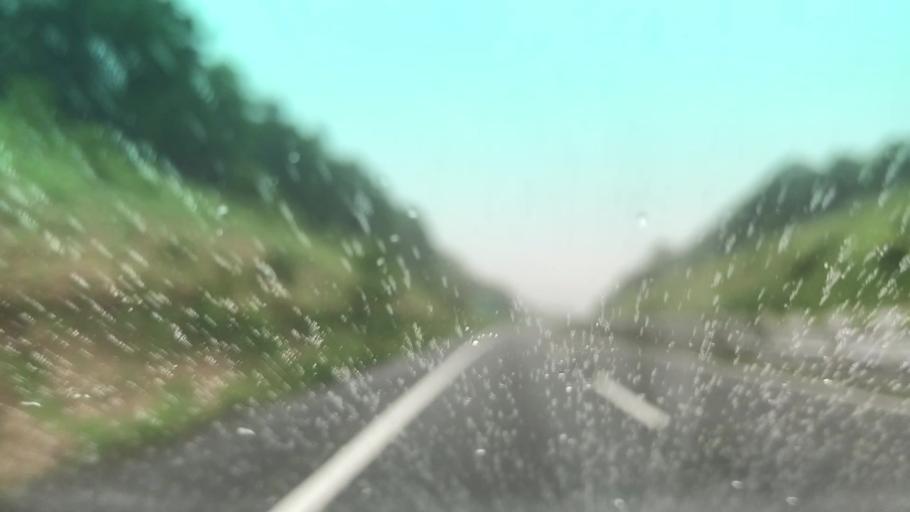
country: JP
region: Hokkaido
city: Tomakomai
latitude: 42.6214
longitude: 141.4781
